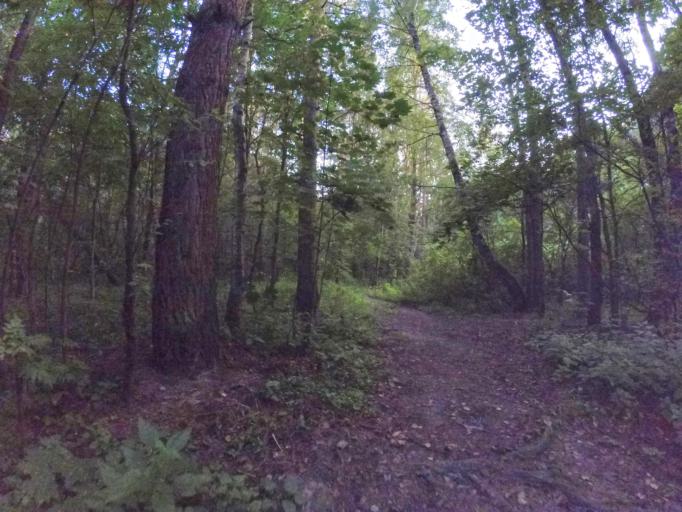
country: RU
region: Moscow
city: Khimki
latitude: 55.8664
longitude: 37.4155
